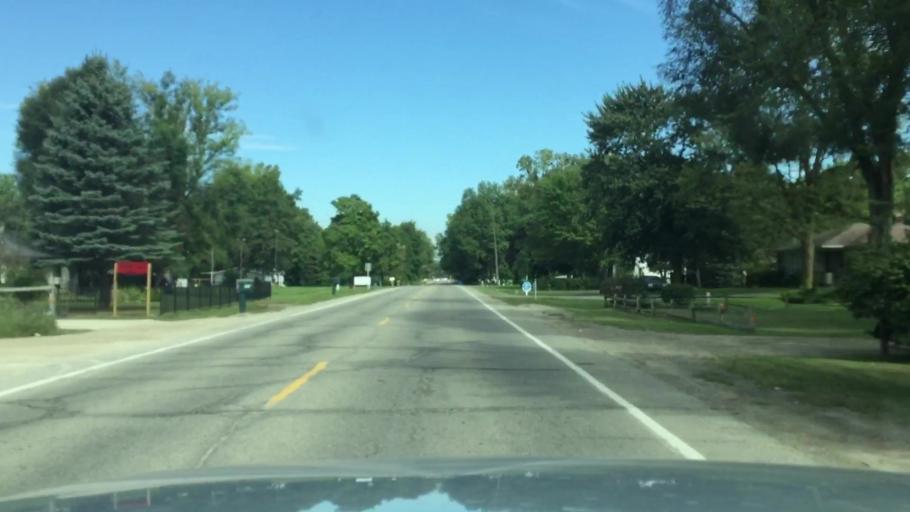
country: US
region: Michigan
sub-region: Wayne County
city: Belleville
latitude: 42.1629
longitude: -83.4824
